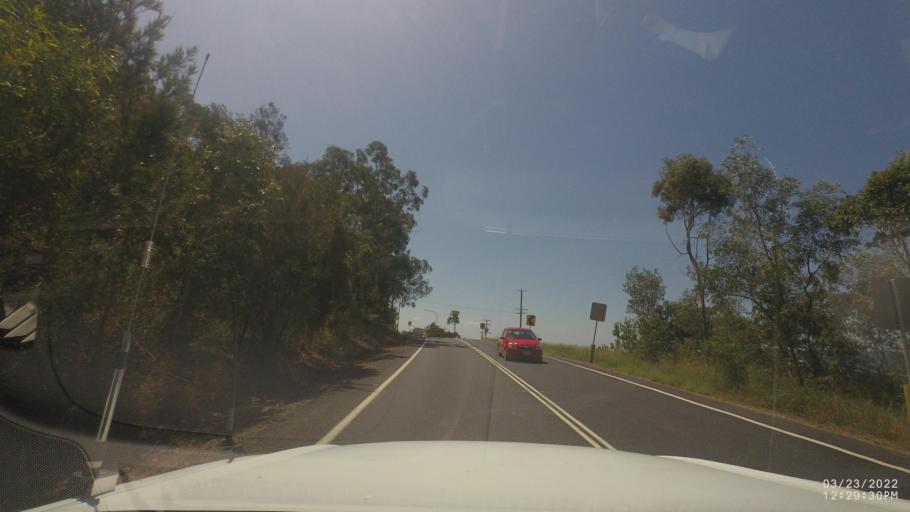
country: AU
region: Queensland
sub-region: Logan
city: Chambers Flat
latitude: -27.8042
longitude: 153.0983
